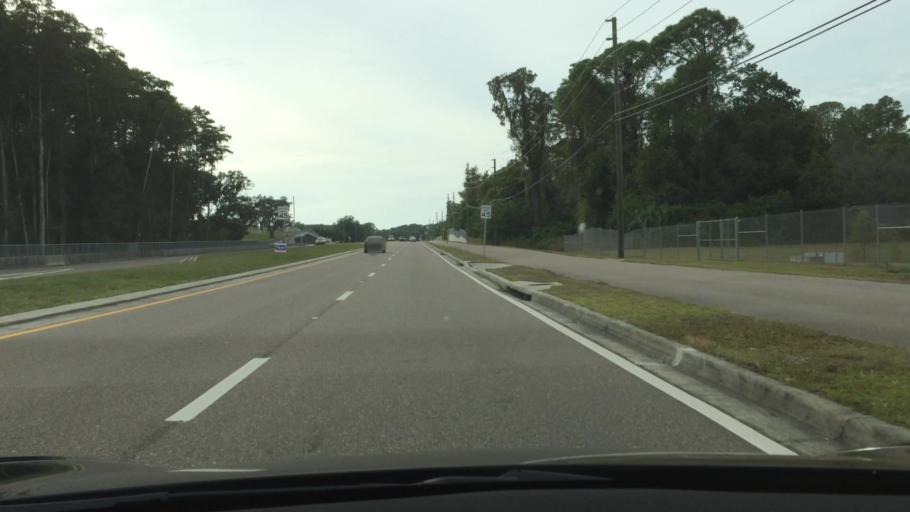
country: US
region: Florida
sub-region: Pasco County
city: Trinity
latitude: 28.1519
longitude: -82.7078
